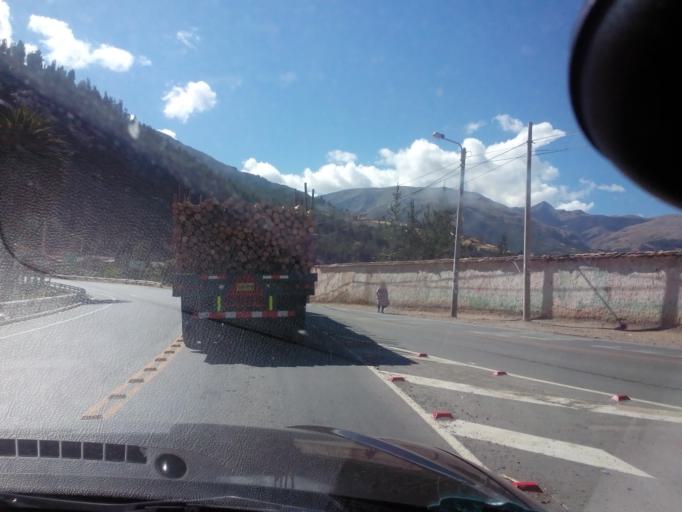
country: PE
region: Cusco
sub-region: Provincia de Quispicanchis
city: Urcos
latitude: -13.6843
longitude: -71.6210
